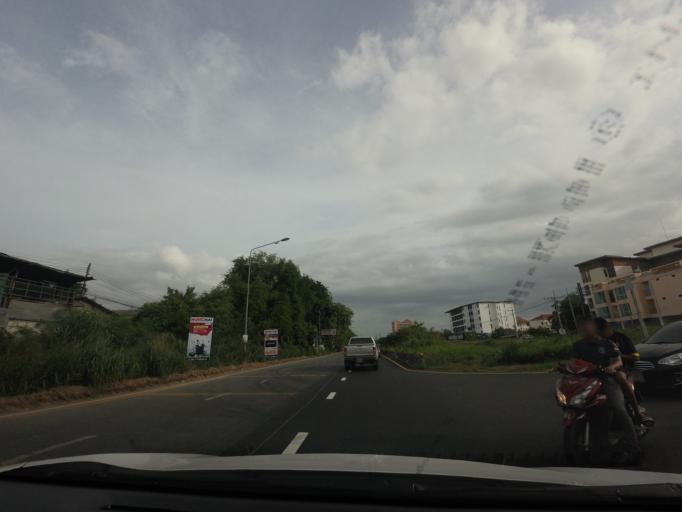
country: TH
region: Chon Buri
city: Phatthaya
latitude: 12.9159
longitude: 100.9023
